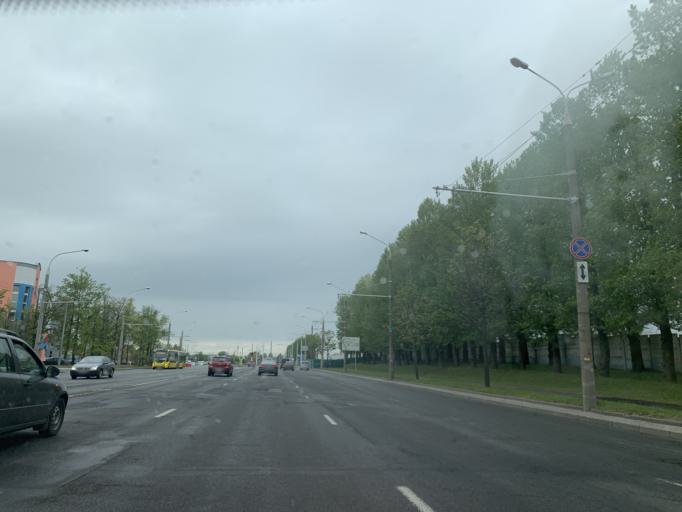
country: BY
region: Minsk
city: Syenitsa
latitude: 53.8660
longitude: 27.5290
